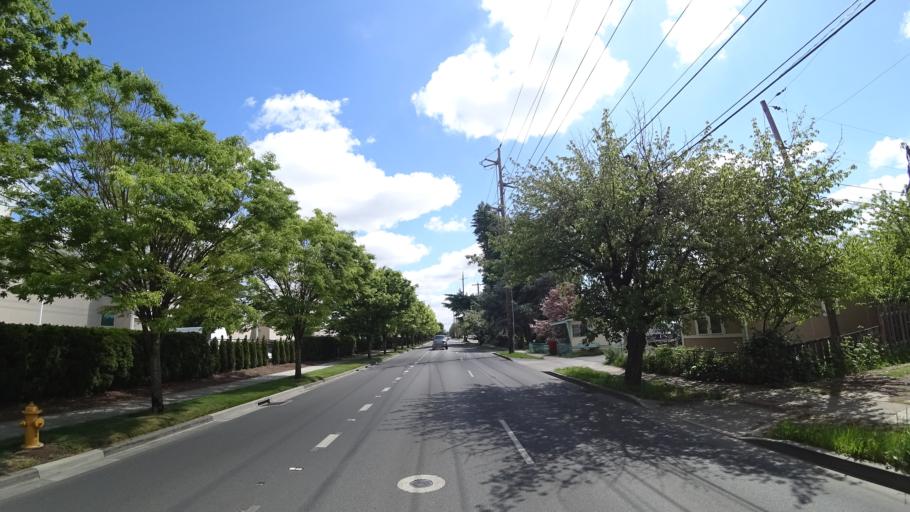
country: US
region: Oregon
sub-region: Washington County
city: Hillsboro
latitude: 45.5201
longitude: -122.9941
